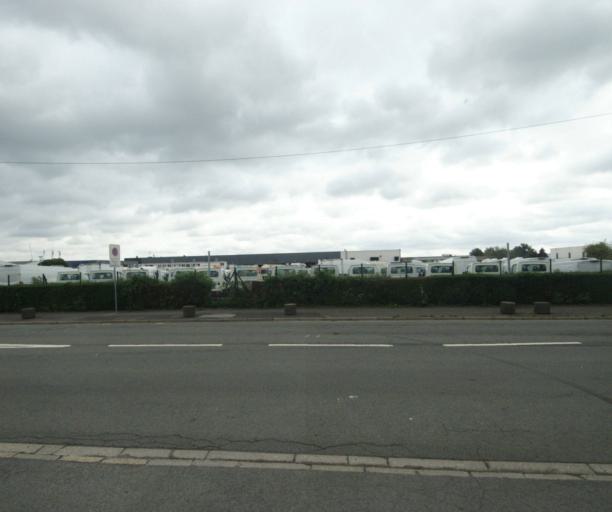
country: FR
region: Nord-Pas-de-Calais
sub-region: Departement du Nord
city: Lesquin
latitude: 50.5800
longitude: 3.1141
